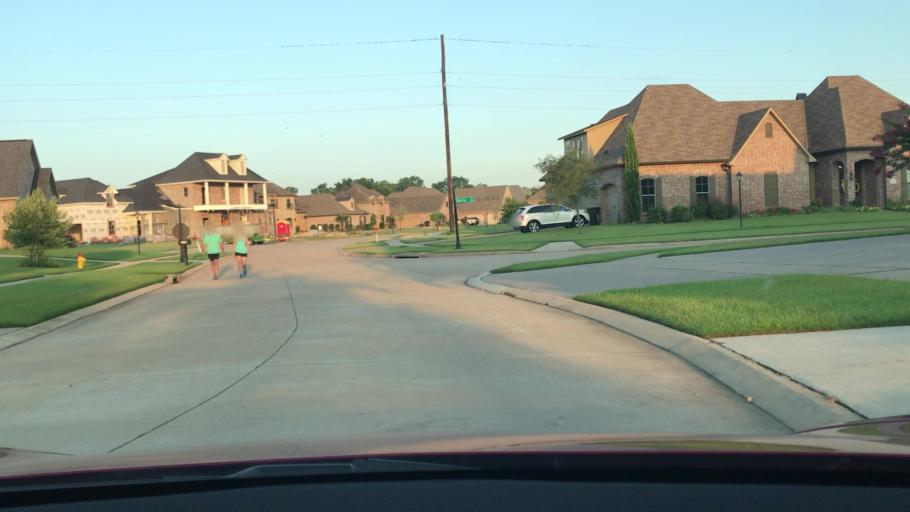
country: US
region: Louisiana
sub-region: Bossier Parish
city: Bossier City
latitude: 32.3905
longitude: -93.7009
